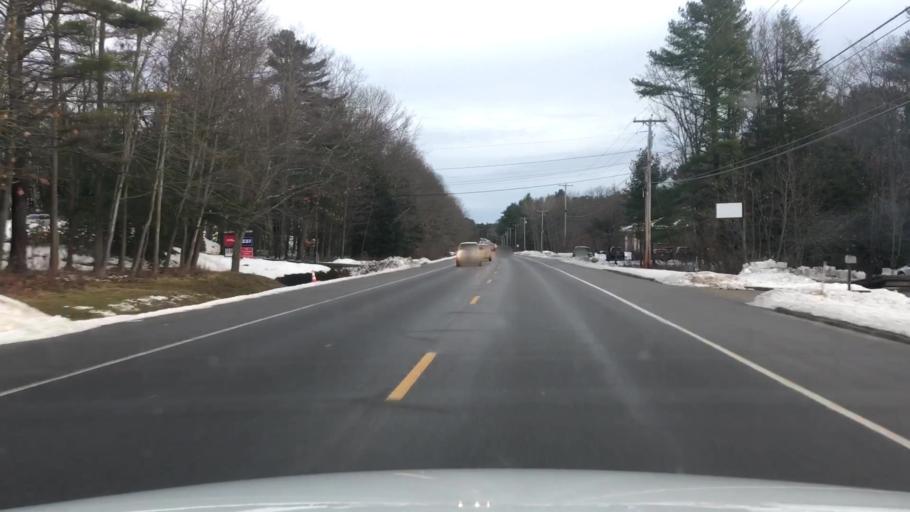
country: US
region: Maine
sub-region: Cumberland County
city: Falmouth Foreside
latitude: 43.7425
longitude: -70.2181
